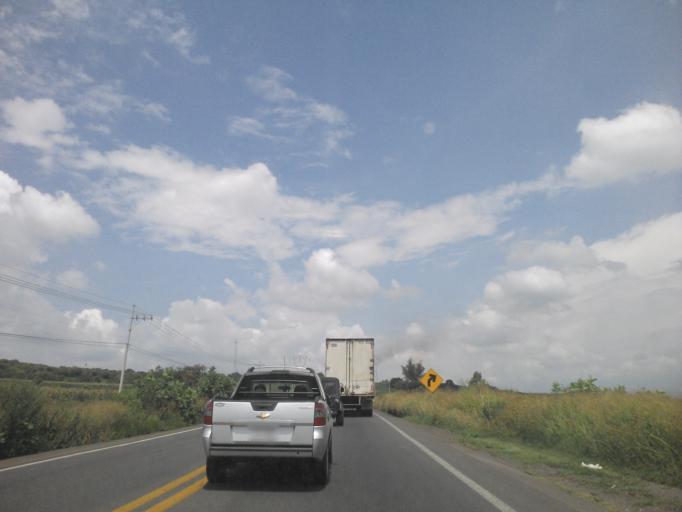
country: MX
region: Jalisco
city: Acatic
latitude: 20.6947
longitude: -102.9805
